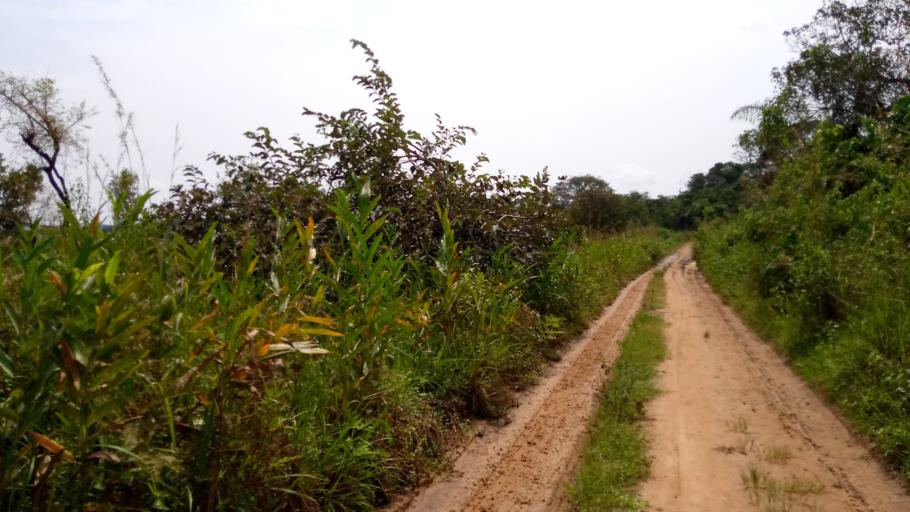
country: CD
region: Bandundu
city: Bandundu
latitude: -4.1360
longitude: 17.4165
